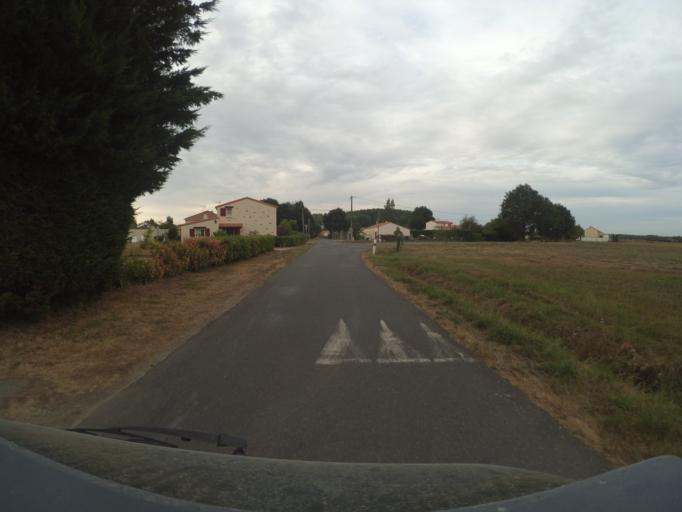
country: FR
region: Pays de la Loire
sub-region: Departement de la Loire-Atlantique
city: Vieillevigne
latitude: 46.9890
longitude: -1.4606
